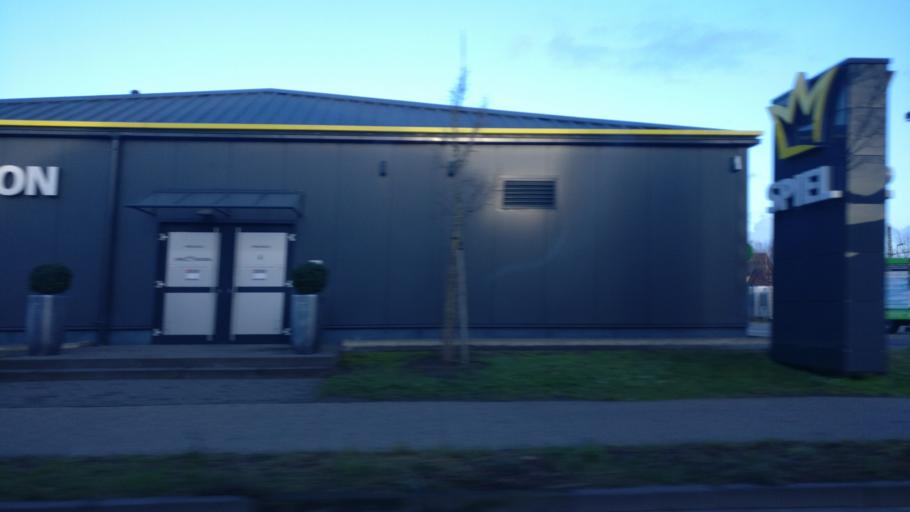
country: DE
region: North Rhine-Westphalia
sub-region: Regierungsbezirk Detmold
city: Lage
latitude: 51.9896
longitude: 8.8018
